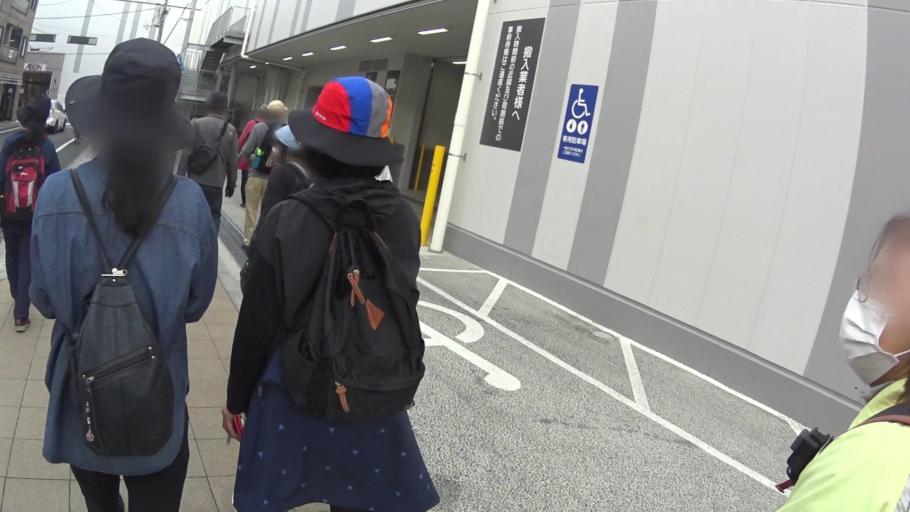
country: JP
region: Osaka
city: Kashihara
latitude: 34.5735
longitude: 135.5930
